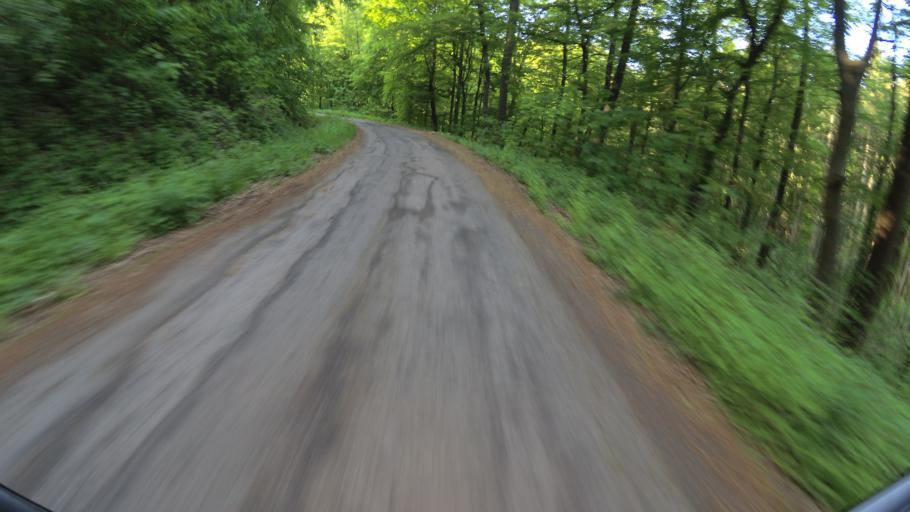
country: DE
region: Saarland
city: Illingen
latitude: 49.4116
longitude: 7.0414
